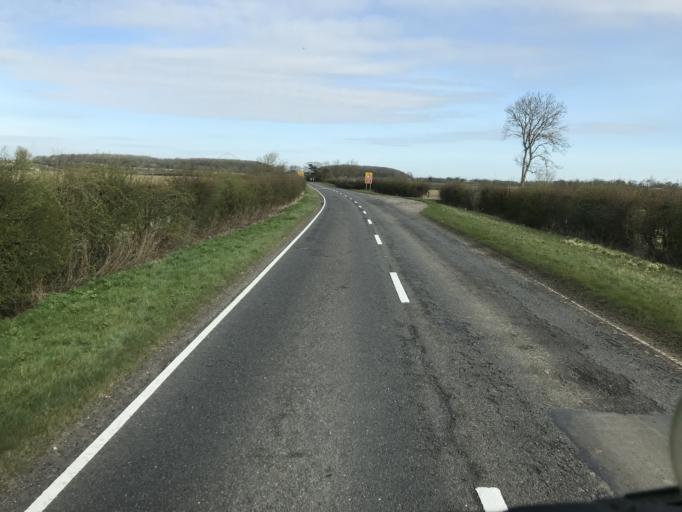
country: GB
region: England
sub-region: Lincolnshire
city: Market Rasen
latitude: 53.3973
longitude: -0.4187
